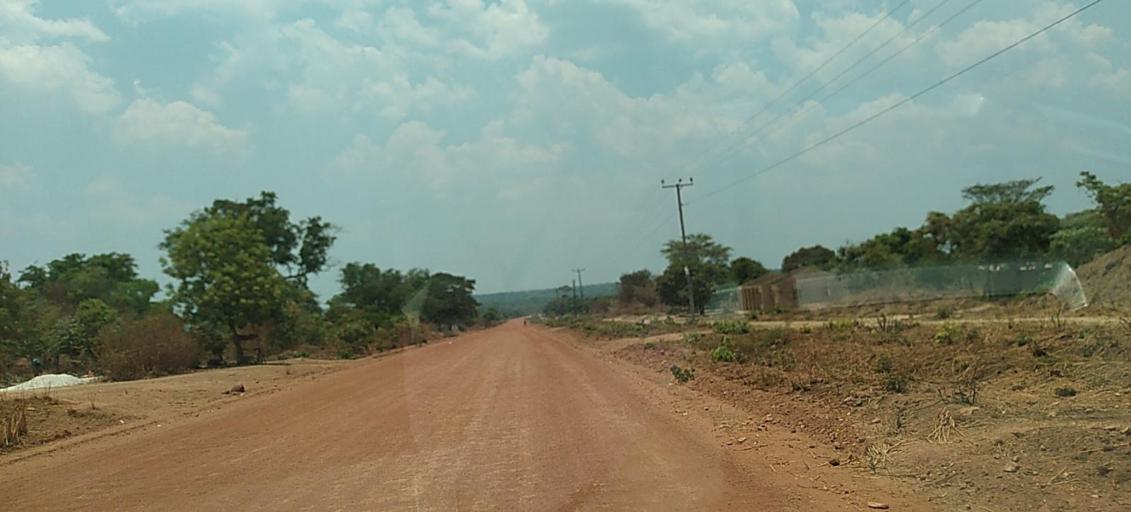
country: ZM
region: Copperbelt
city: Chingola
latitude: -12.8750
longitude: 27.5951
